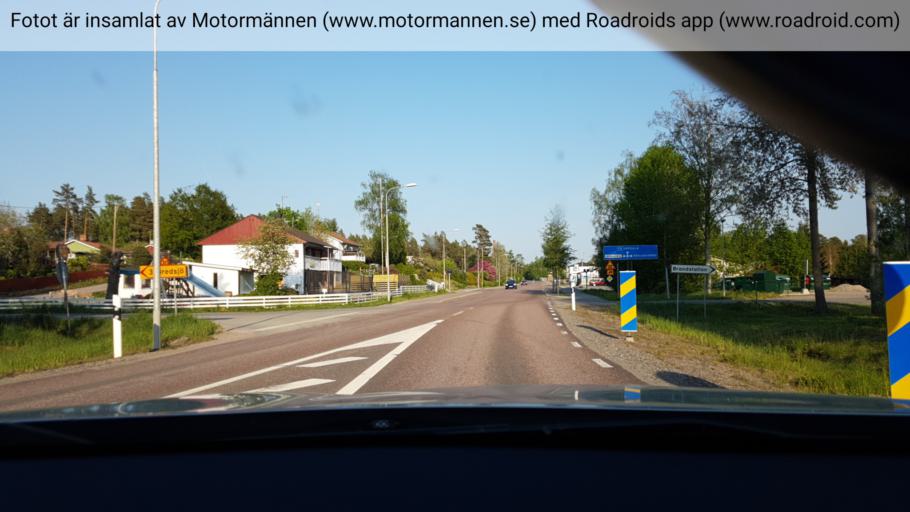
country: SE
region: Uppsala
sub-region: Enkopings Kommun
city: Orsundsbro
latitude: 59.8886
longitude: 17.1829
